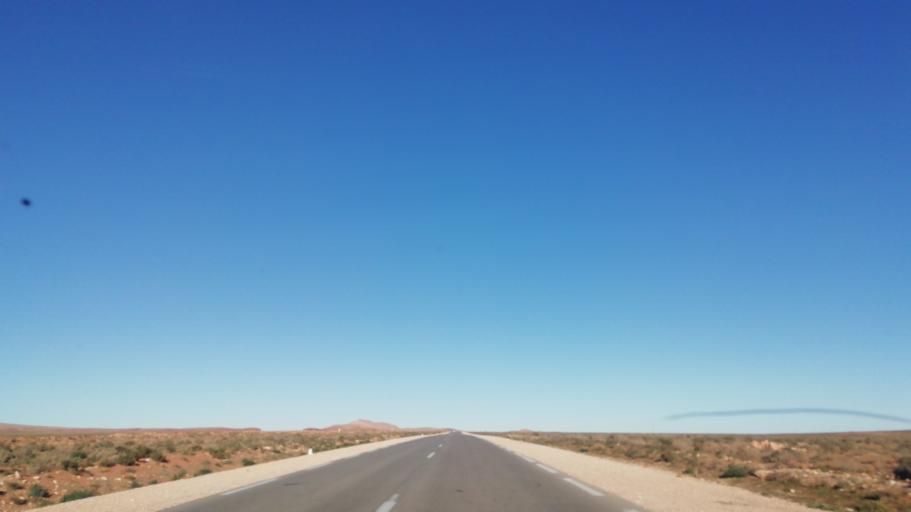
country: DZ
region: El Bayadh
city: El Abiodh Sidi Cheikh
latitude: 33.1013
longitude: 0.2103
